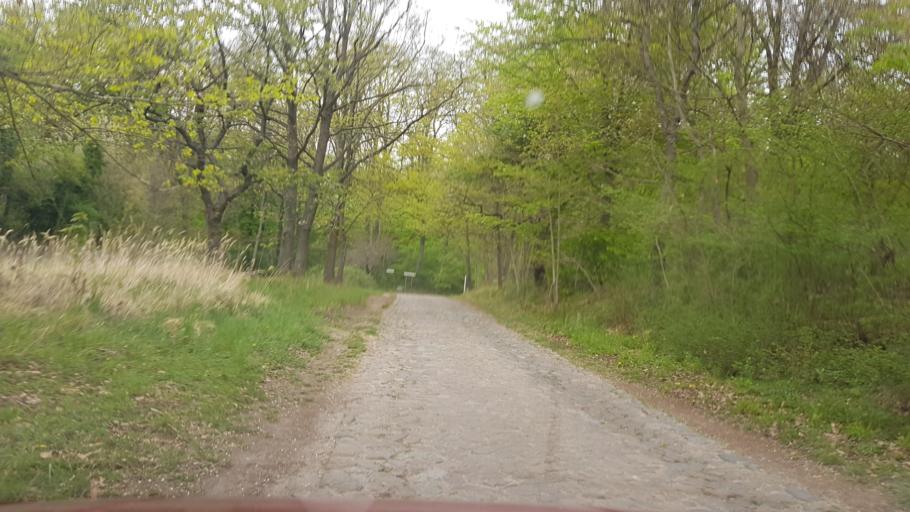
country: PL
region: West Pomeranian Voivodeship
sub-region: Powiat gryfinski
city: Stare Czarnowo
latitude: 53.2961
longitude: 14.7253
